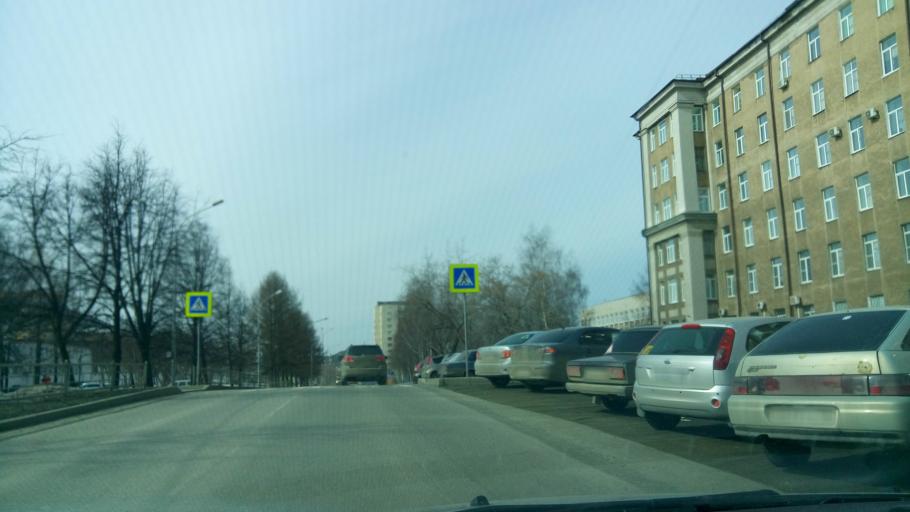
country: RU
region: Sverdlovsk
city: Nizhniy Tagil
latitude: 57.9054
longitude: 59.9689
